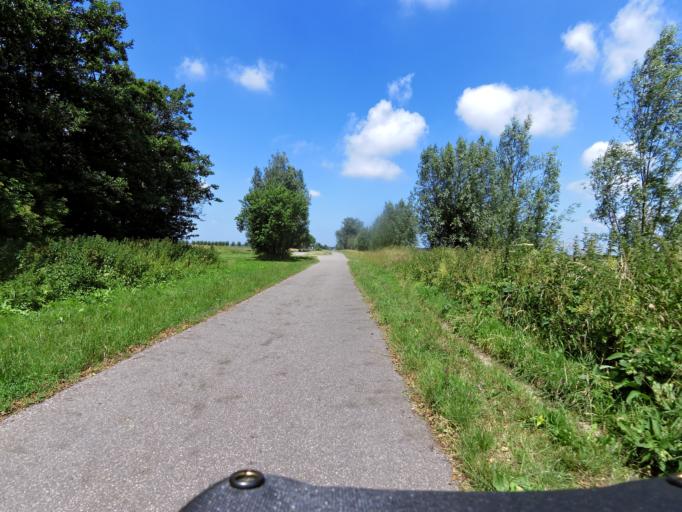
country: NL
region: South Holland
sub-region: Gemeente Schiedam
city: Schiedam
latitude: 51.9555
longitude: 4.3684
